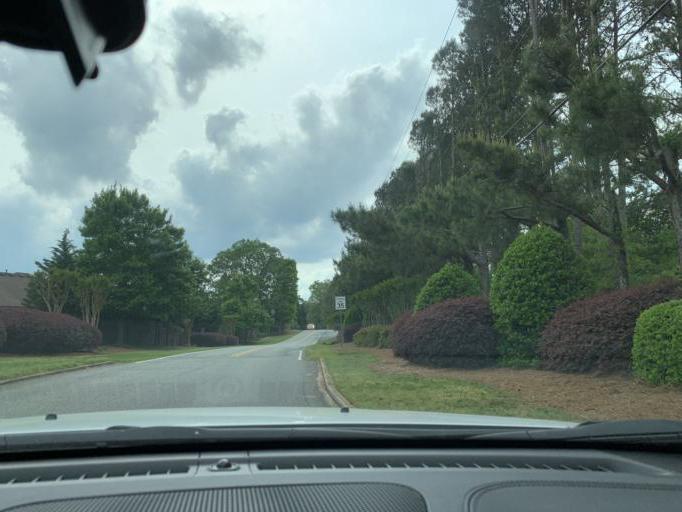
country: US
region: Georgia
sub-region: Gwinnett County
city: Suwanee
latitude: 34.1012
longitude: -84.1189
